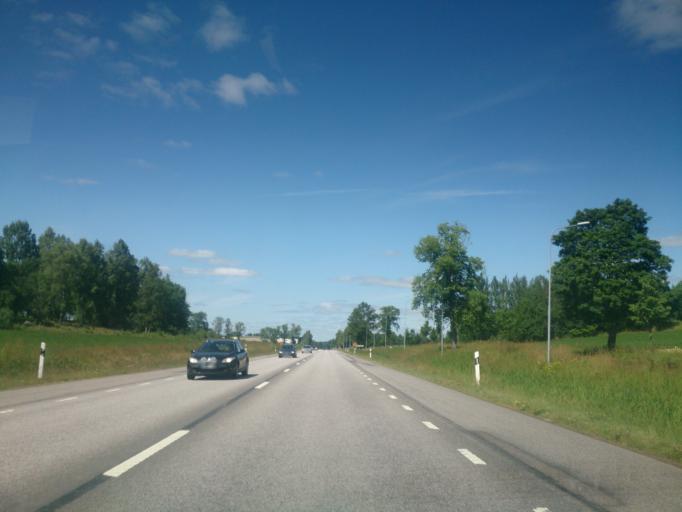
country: SE
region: OEstergoetland
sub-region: Atvidabergs Kommun
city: Atvidaberg
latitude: 58.2215
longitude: 15.9713
